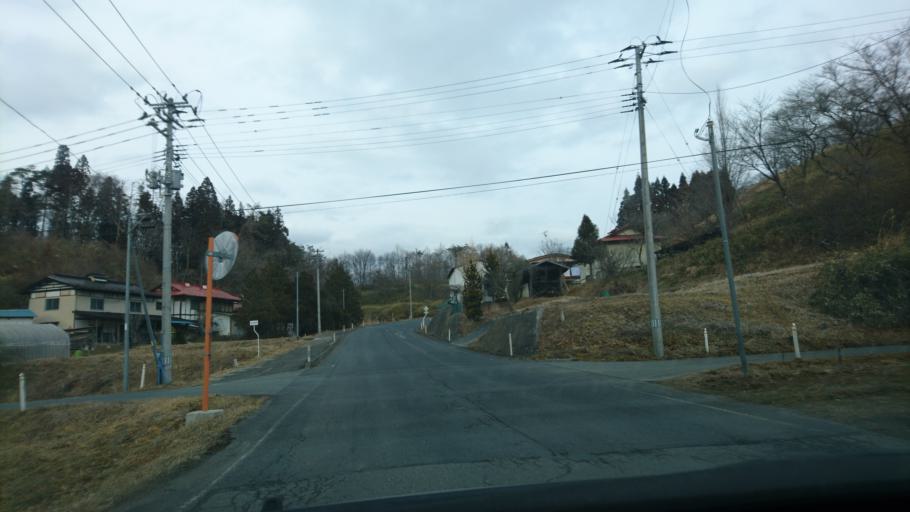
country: JP
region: Iwate
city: Ichinoseki
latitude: 38.9457
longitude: 141.3611
